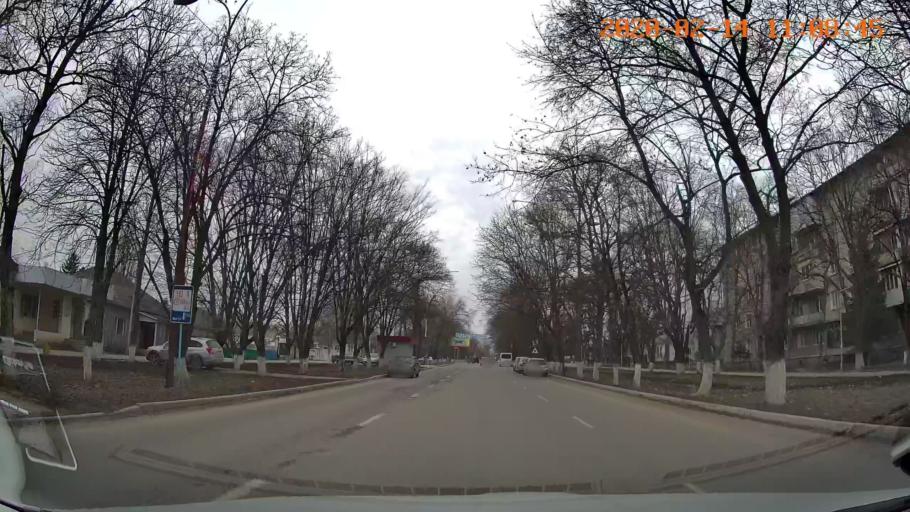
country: MD
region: Raionul Edinet
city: Edinet
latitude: 48.1739
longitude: 27.2993
